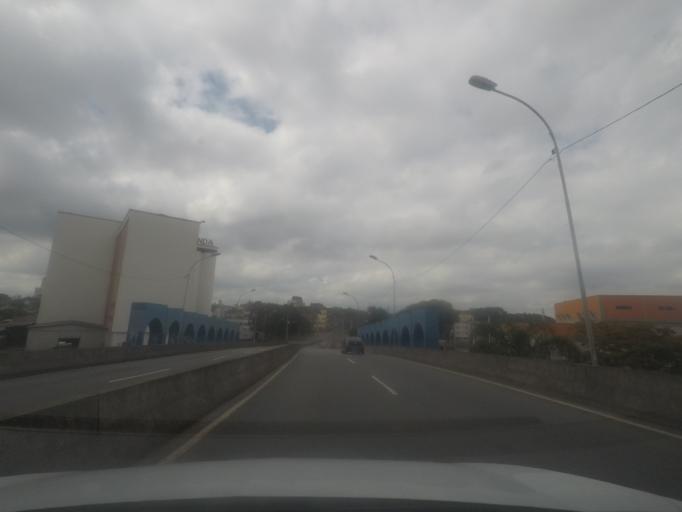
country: BR
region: Parana
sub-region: Curitiba
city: Curitiba
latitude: -25.4362
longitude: -49.2535
